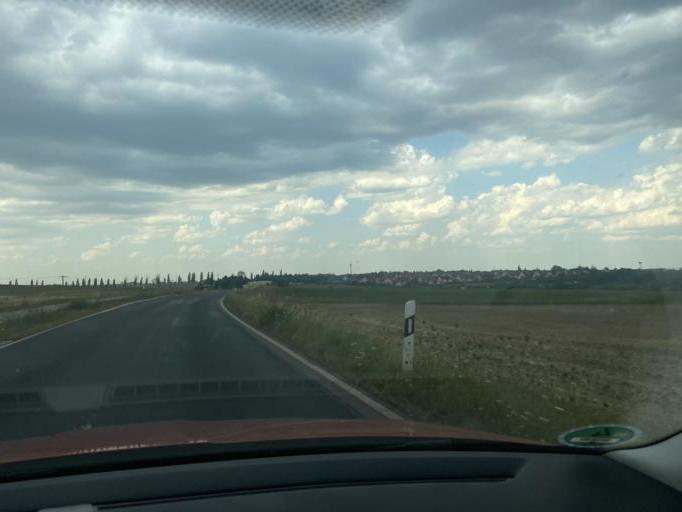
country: DE
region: Saxony
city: Tharandt
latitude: 51.0231
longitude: 13.5824
